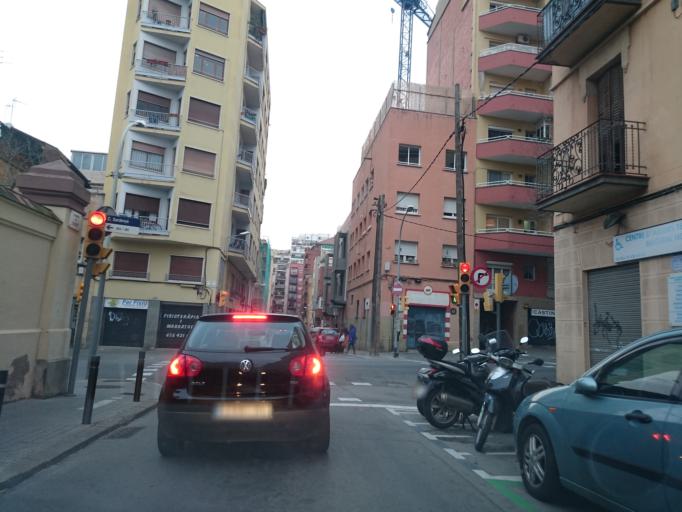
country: ES
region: Catalonia
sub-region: Provincia de Barcelona
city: Horta-Guinardo
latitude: 41.4091
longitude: 2.1661
